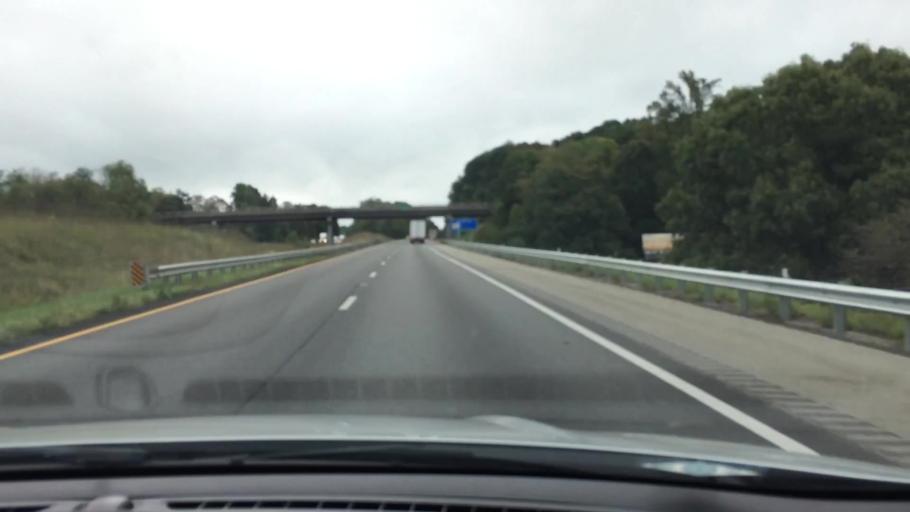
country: US
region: Virginia
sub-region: City of Radford
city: Radford
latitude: 37.0988
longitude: -80.5392
